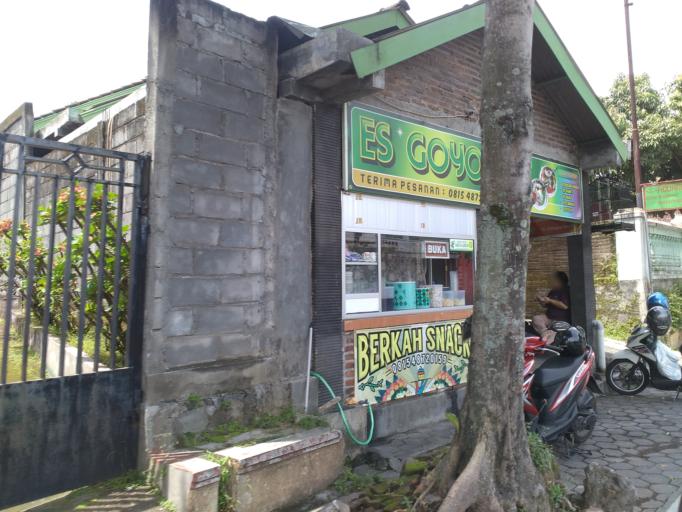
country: ID
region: Central Java
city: Boyolali
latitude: -7.5398
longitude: 110.6036
